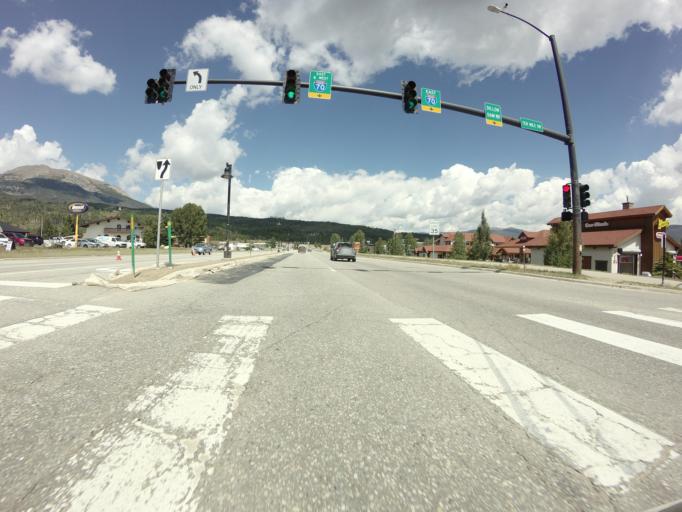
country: US
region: Colorado
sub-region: Summit County
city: Frisco
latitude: 39.5881
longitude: -106.0950
